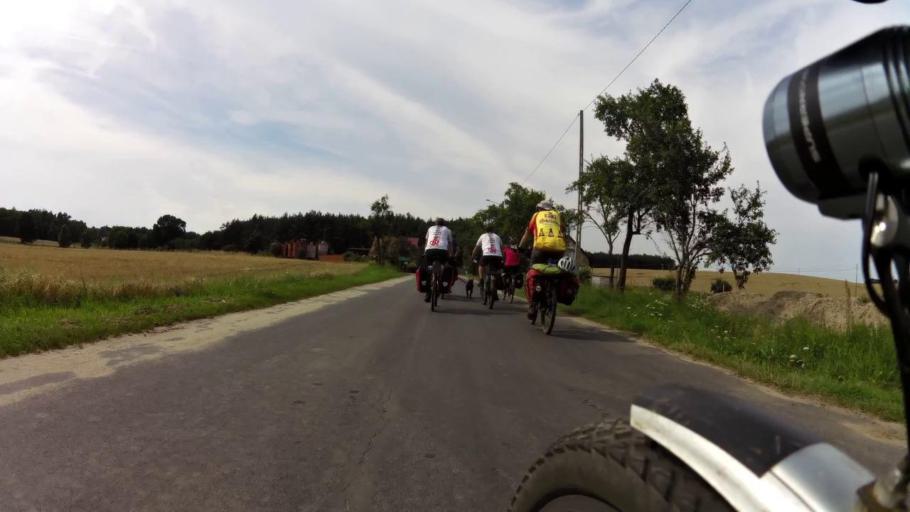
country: PL
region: West Pomeranian Voivodeship
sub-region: Powiat mysliborski
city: Debno
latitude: 52.7876
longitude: 14.6888
